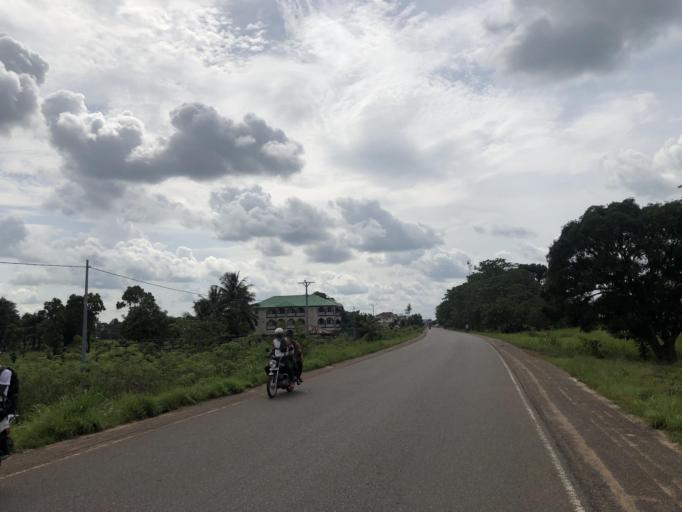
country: SL
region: Northern Province
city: Magburaka
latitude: 8.7157
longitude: -11.9287
